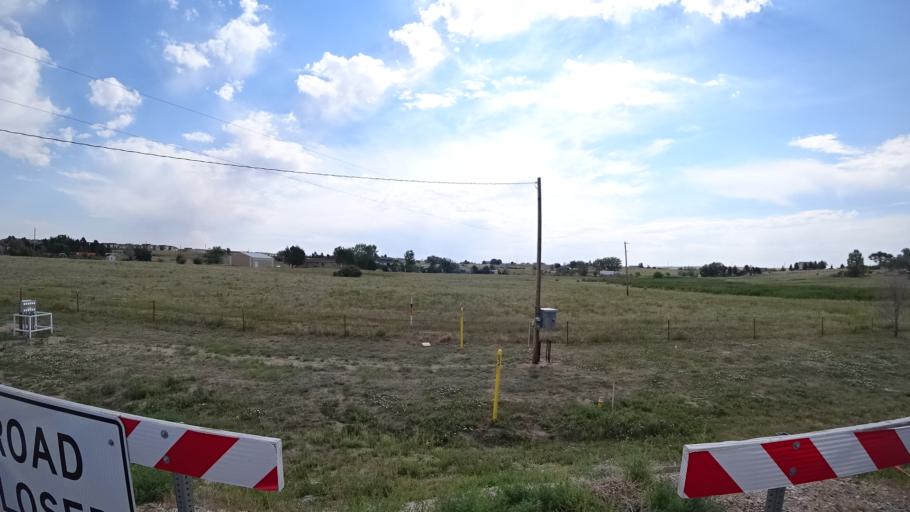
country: US
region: Colorado
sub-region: El Paso County
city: Cimarron Hills
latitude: 38.9235
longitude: -104.6806
